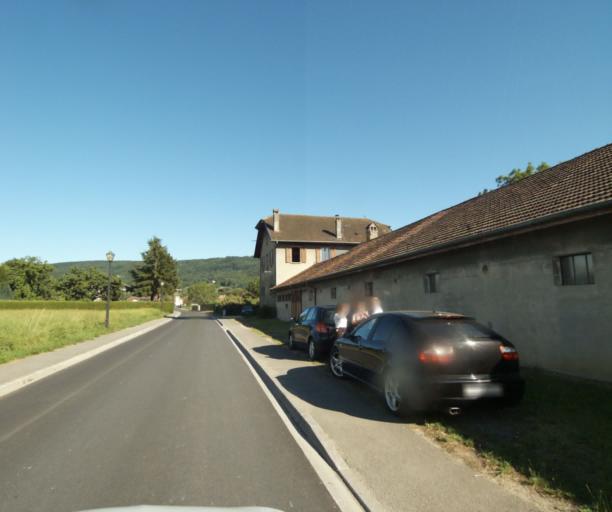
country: FR
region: Rhone-Alpes
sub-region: Departement de la Haute-Savoie
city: Massongy
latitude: 46.3209
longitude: 6.3262
